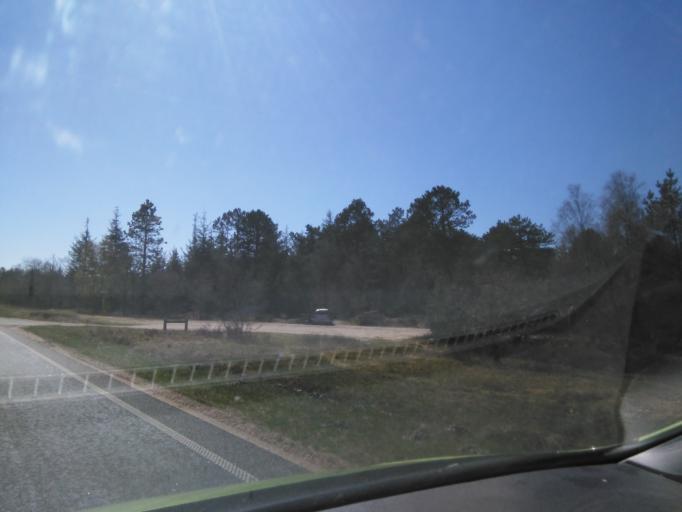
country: DK
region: South Denmark
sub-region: Varde Kommune
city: Oksbol
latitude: 55.6000
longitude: 8.2246
